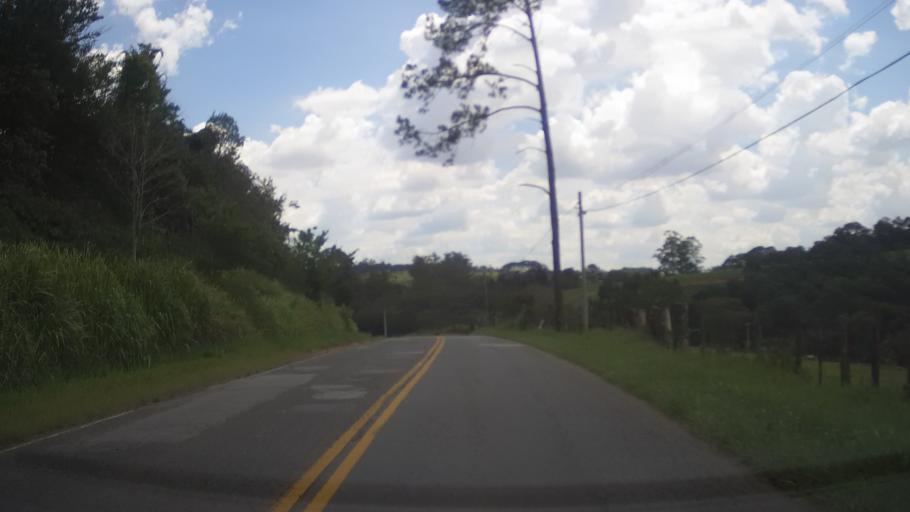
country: BR
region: Sao Paulo
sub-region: Campo Limpo Paulista
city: Campo Limpo Paulista
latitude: -23.1440
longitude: -46.8026
